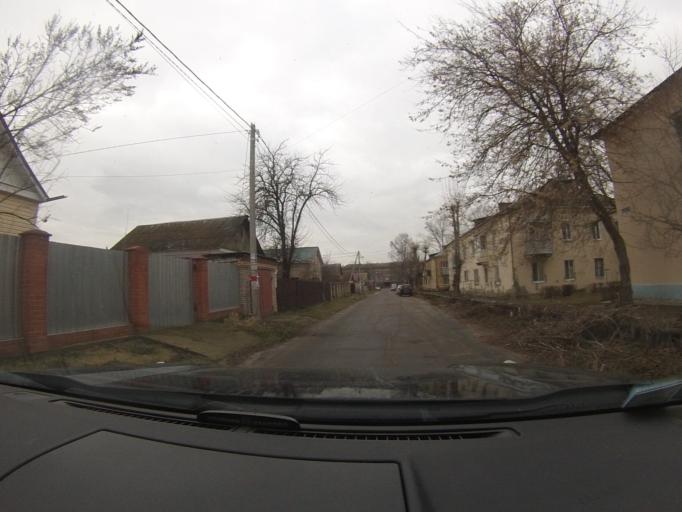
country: RU
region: Moskovskaya
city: Lopatinskiy
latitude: 55.3387
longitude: 38.7229
